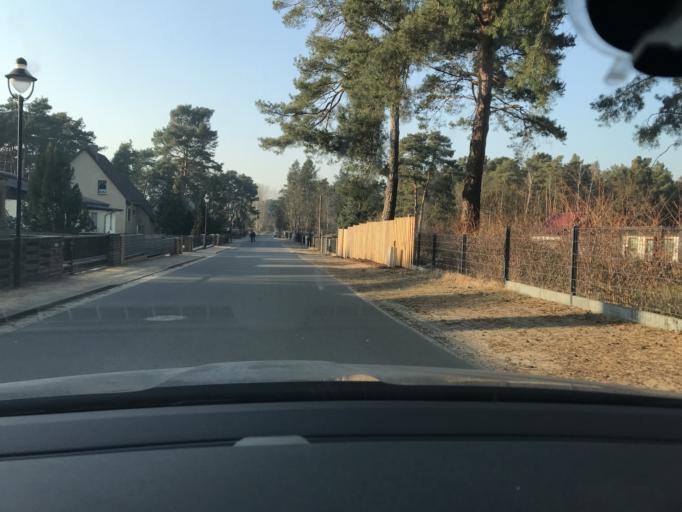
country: DE
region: Brandenburg
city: Munchehofe
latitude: 52.2151
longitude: 13.7826
